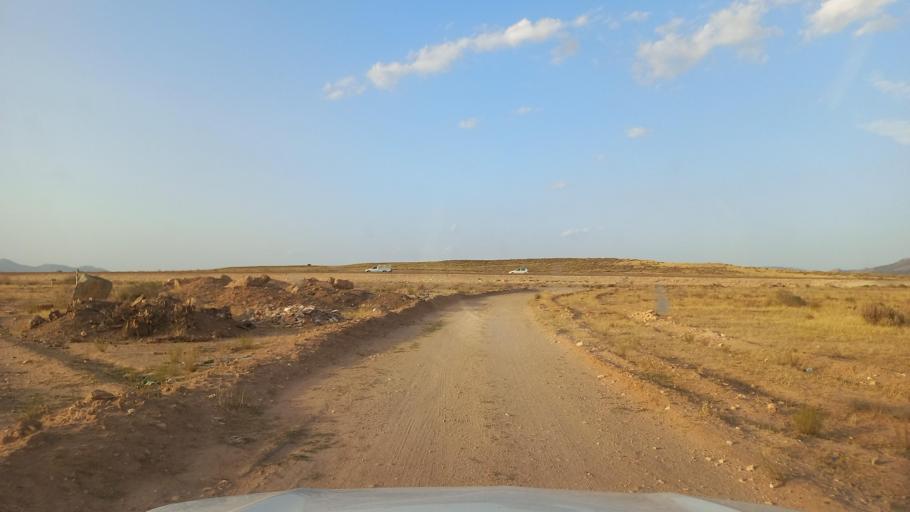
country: TN
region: Al Qasrayn
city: Sbiba
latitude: 35.3085
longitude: 9.0736
